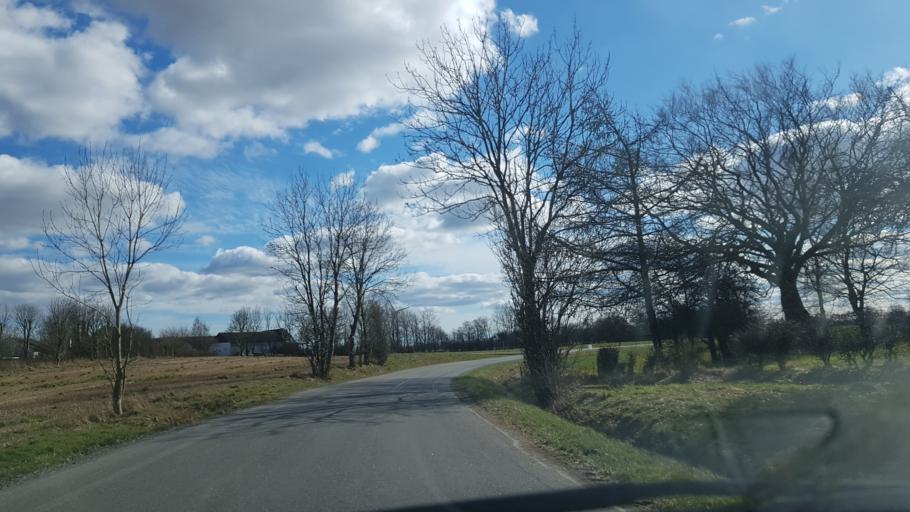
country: DK
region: South Denmark
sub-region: Kolding Kommune
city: Vamdrup
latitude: 55.3844
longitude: 9.2934
